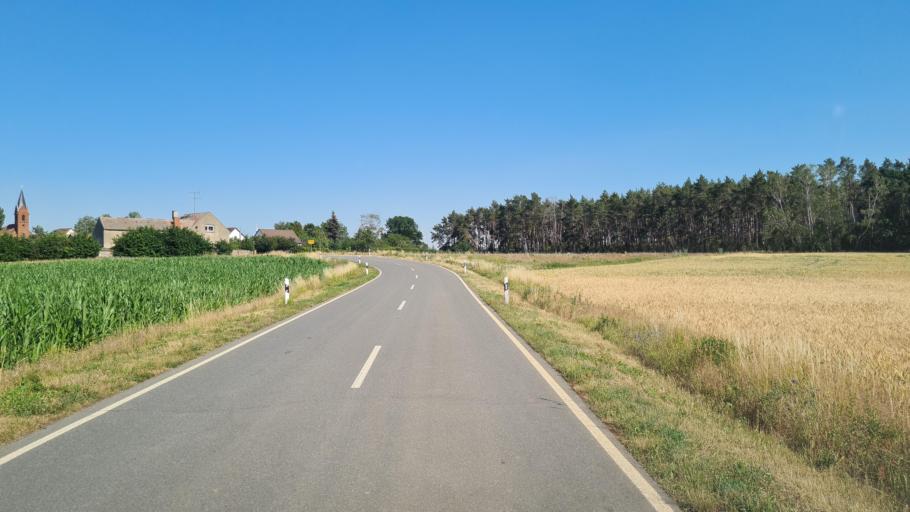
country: DE
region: Saxony-Anhalt
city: Prettin
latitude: 51.6934
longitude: 12.9132
